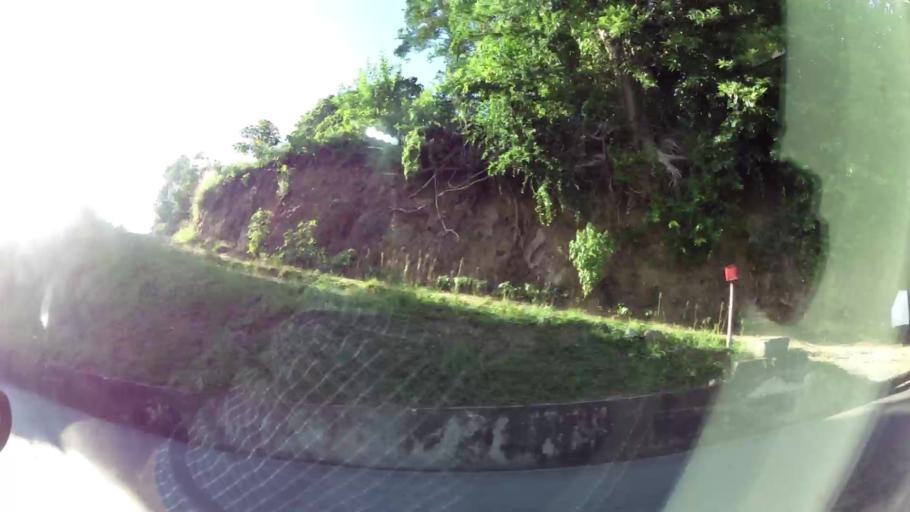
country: TT
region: Tobago
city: Scarborough
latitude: 11.1924
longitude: -60.6827
